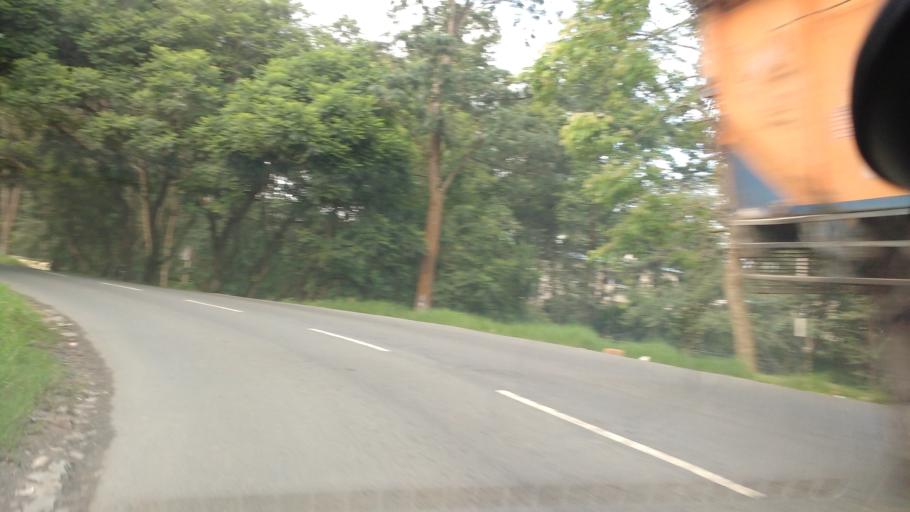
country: IN
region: Meghalaya
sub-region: East Khasi Hills
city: Shillong
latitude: 25.5717
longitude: 91.8658
